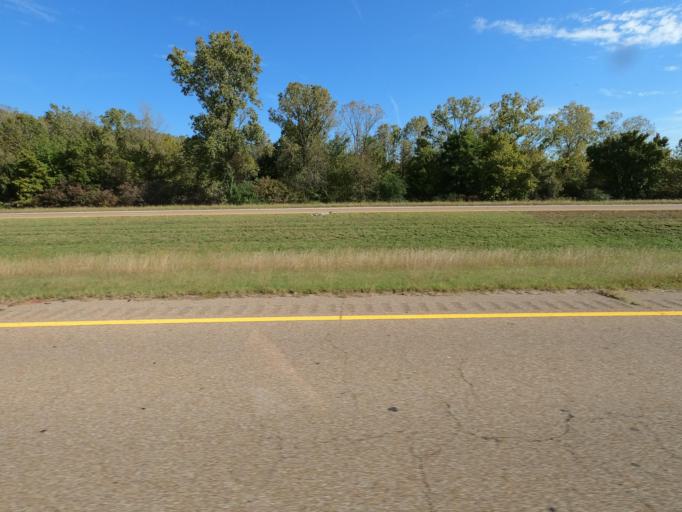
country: US
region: Tennessee
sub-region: Shelby County
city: Millington
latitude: 35.3261
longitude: -89.8858
